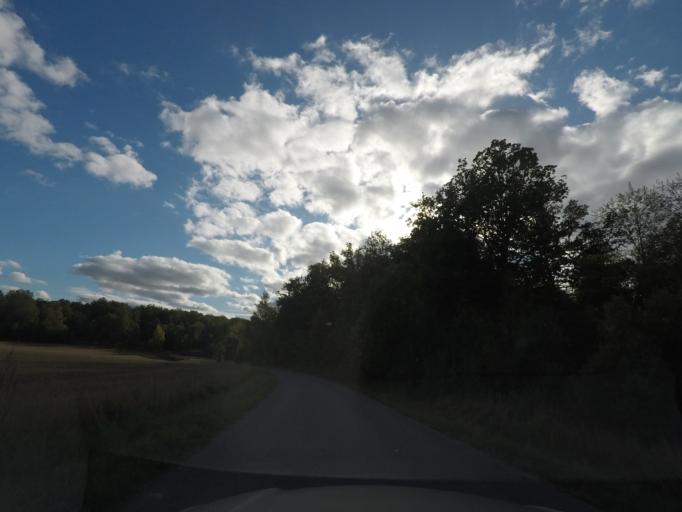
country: SE
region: Vaestmanland
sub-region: Kungsors Kommun
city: Kungsoer
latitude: 59.4855
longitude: 16.1816
